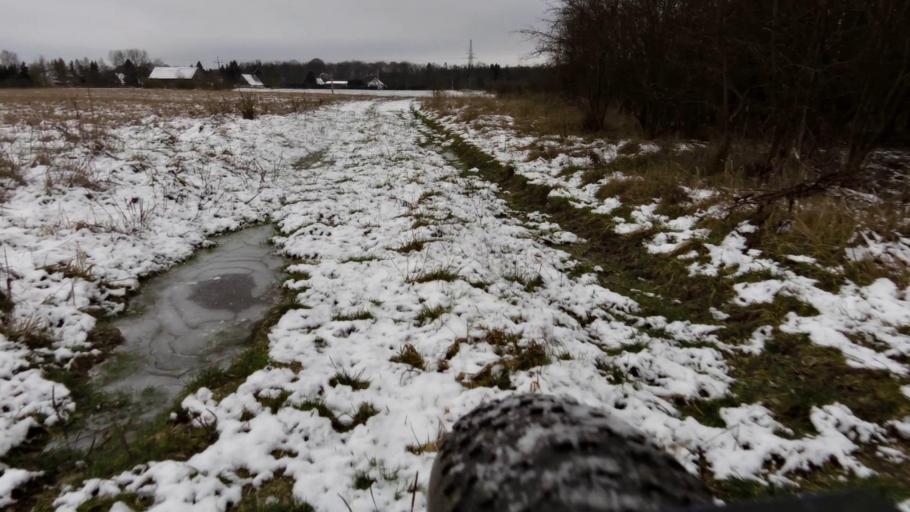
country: PL
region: West Pomeranian Voivodeship
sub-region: Powiat walecki
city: Miroslawiec
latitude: 53.3438
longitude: 16.2685
